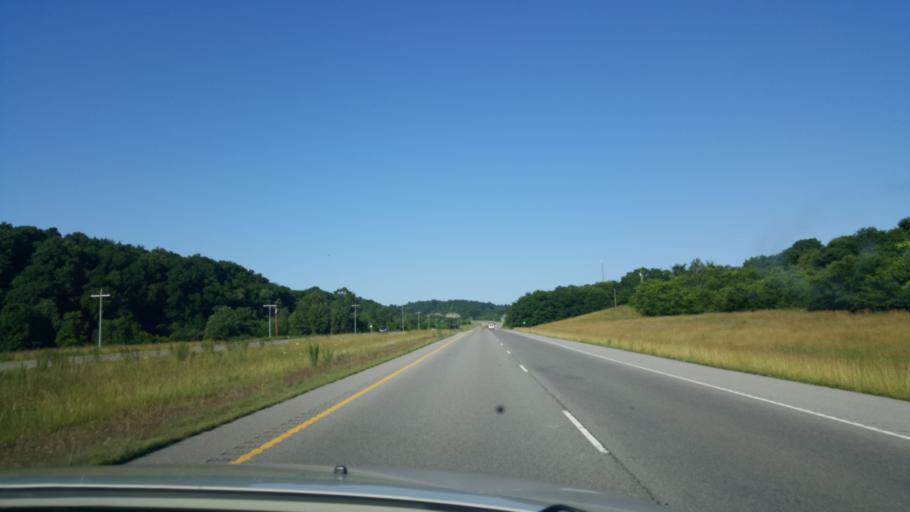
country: US
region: Tennessee
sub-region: Maury County
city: Mount Pleasant
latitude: 35.4884
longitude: -87.2425
